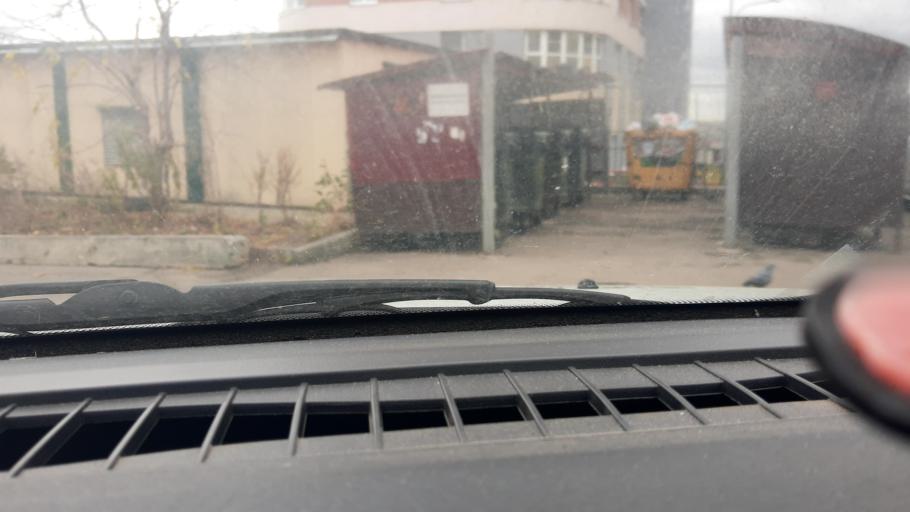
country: RU
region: Nizjnij Novgorod
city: Nizhniy Novgorod
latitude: 56.2832
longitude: 44.0353
